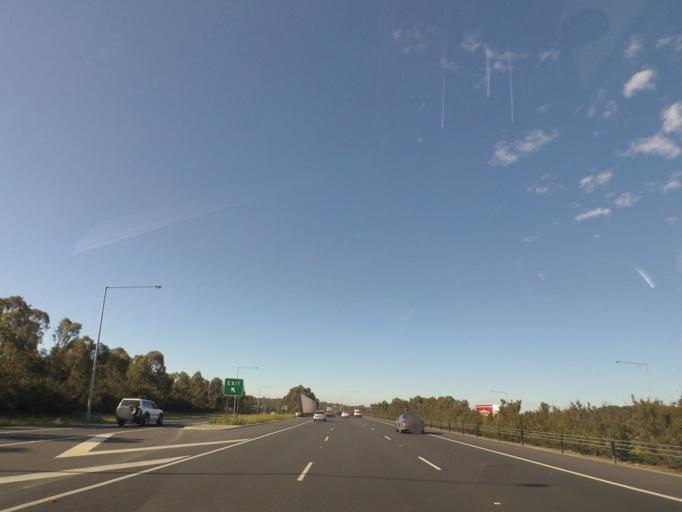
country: AU
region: Victoria
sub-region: Knox
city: Wantirna South
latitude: -37.8731
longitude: 145.2120
